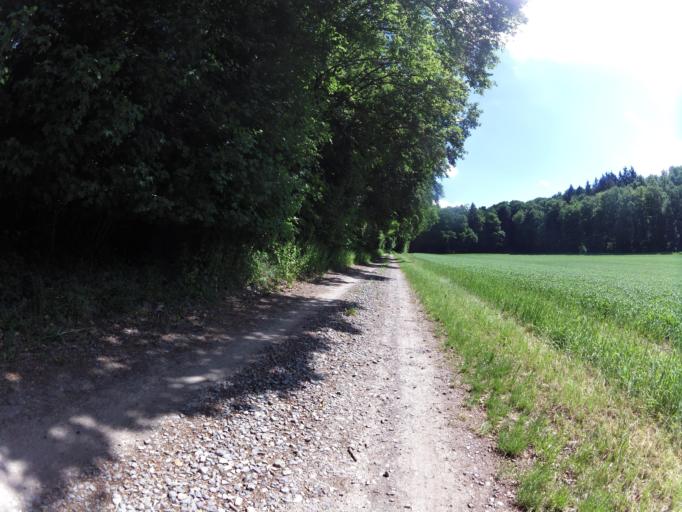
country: DE
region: Bavaria
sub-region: Regierungsbezirk Unterfranken
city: Uettingen
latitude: 49.7808
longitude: 9.7513
